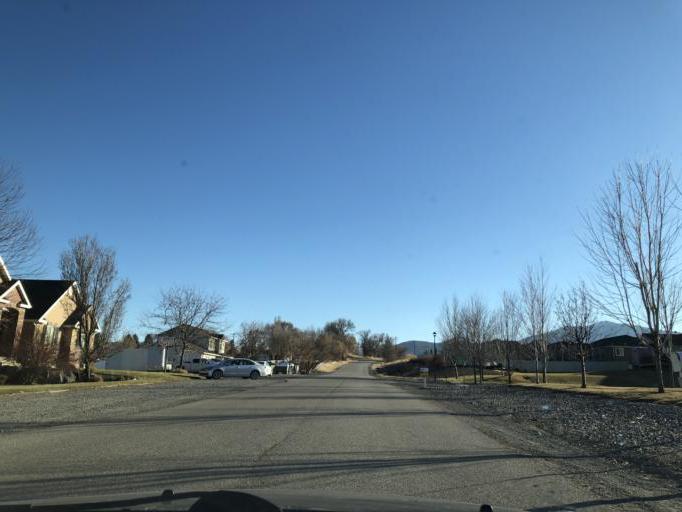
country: US
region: Utah
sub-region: Cache County
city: Wellsville
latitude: 41.6107
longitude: -111.9310
